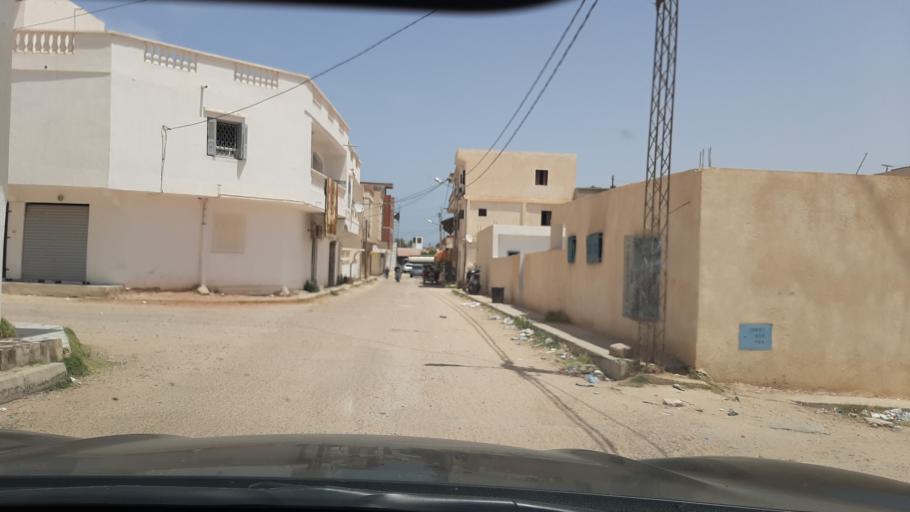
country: TN
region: Qabis
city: Matmata
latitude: 33.6175
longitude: 10.2838
